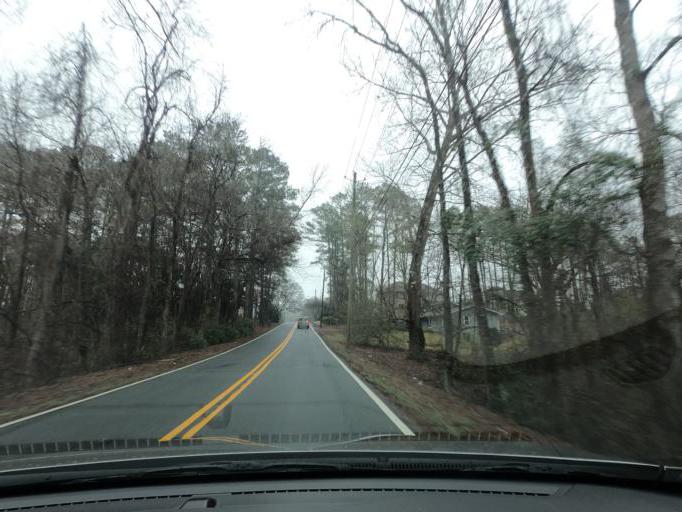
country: US
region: Georgia
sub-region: Fulton County
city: Alpharetta
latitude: 34.0925
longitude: -84.3332
